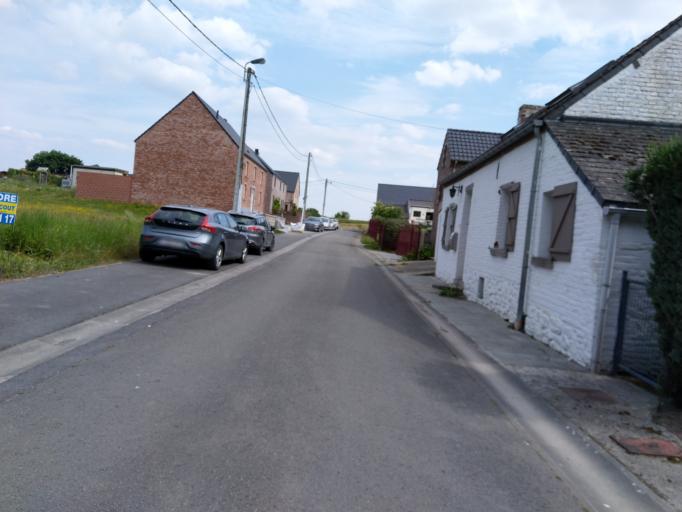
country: BE
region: Wallonia
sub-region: Province du Hainaut
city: Lens
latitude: 50.5815
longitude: 3.9346
